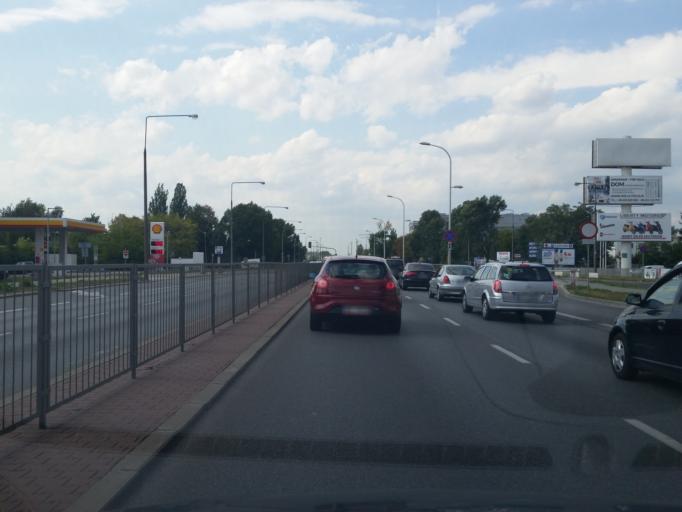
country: PL
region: Masovian Voivodeship
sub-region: Warszawa
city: Wlochy
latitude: 52.1927
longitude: 20.9457
